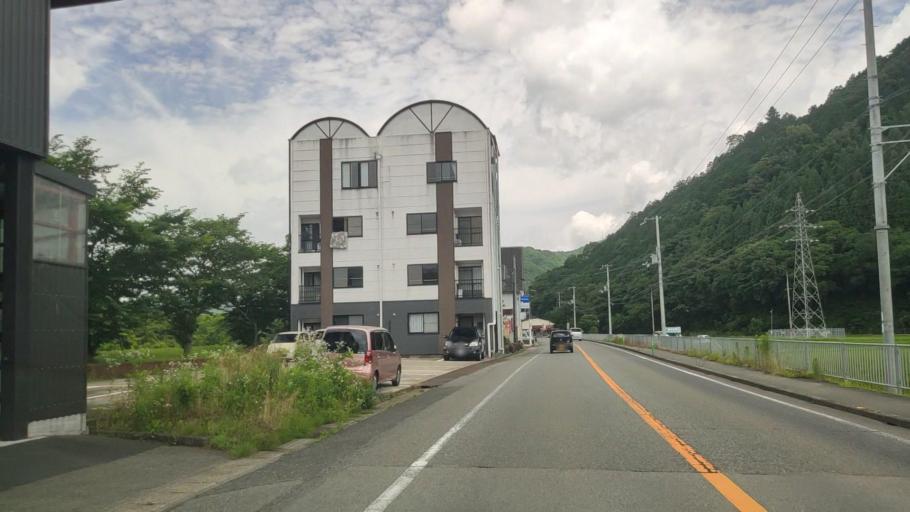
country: JP
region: Hyogo
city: Toyooka
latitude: 35.3484
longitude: 134.8429
